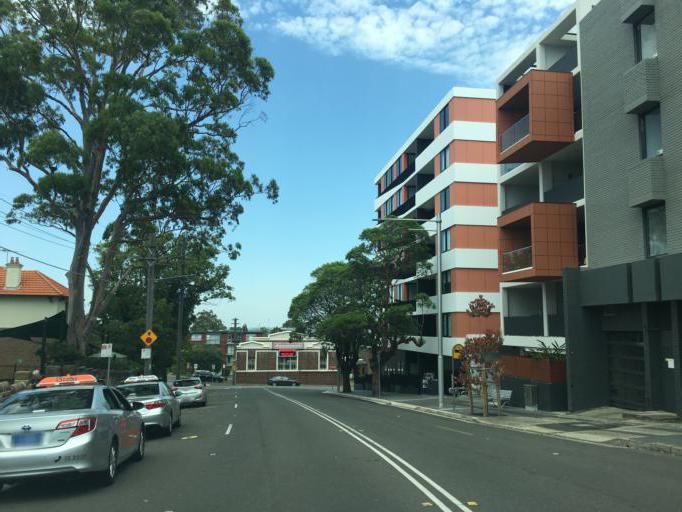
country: AU
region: New South Wales
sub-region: Hunters Hill
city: Gladesville
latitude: -33.8303
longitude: 151.1265
